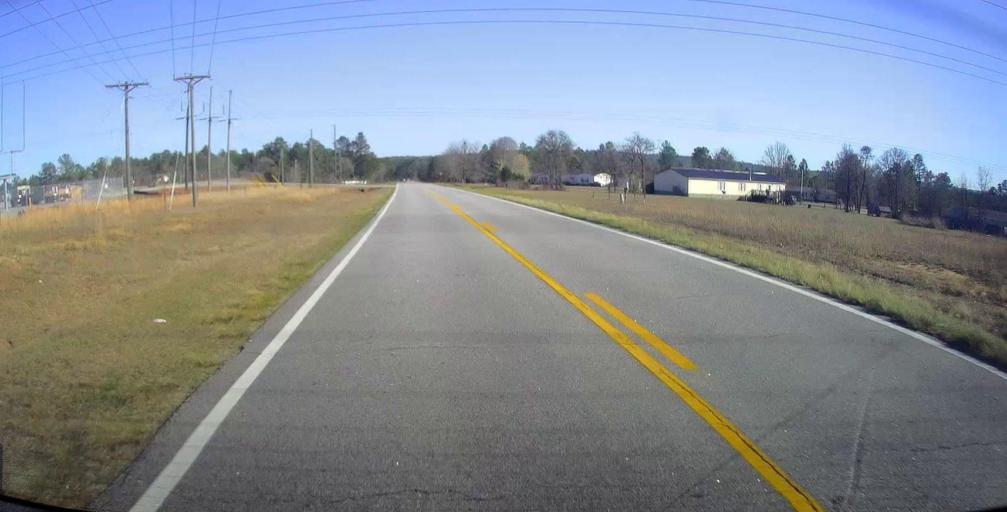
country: US
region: Georgia
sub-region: Peach County
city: Byron
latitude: 32.6952
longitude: -83.7741
